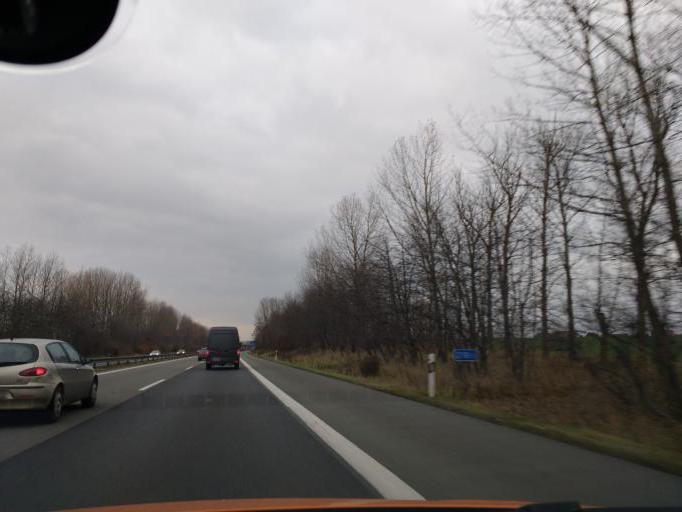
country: DE
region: Brandenburg
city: Fehrbellin
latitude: 52.7971
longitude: 12.7955
